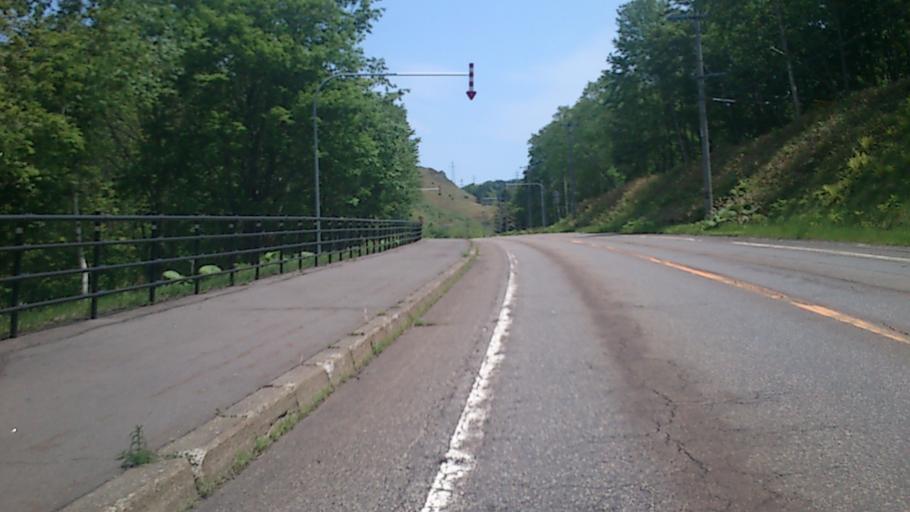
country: JP
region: Hokkaido
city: Otofuke
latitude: 43.3606
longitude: 143.2488
